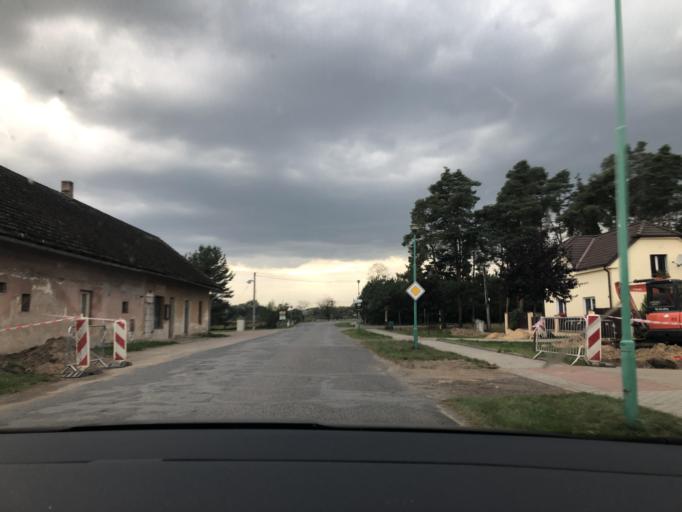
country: CZ
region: Pardubicky
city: Chvaletice
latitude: 50.0513
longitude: 15.4069
